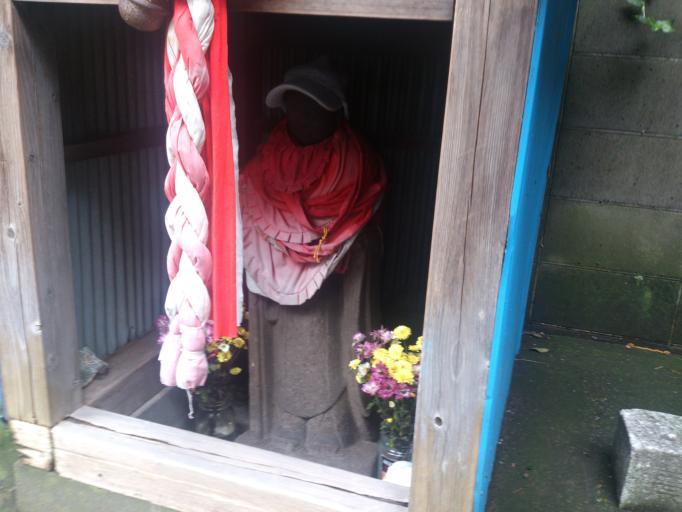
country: JP
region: Chiba
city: Chiba
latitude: 35.6421
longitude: 140.0731
